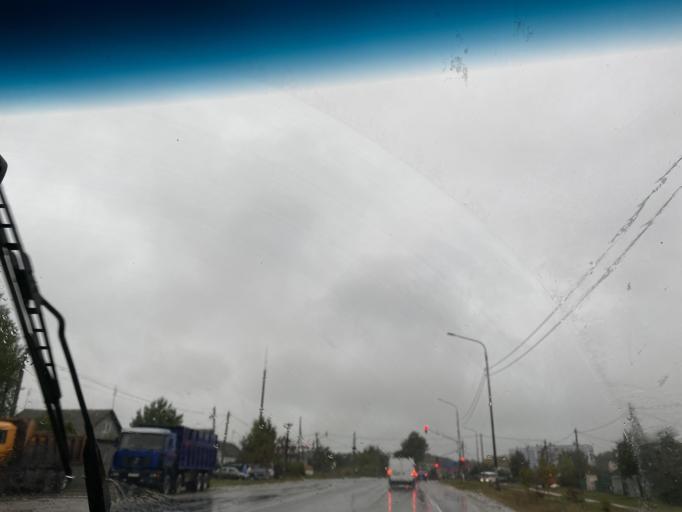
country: RU
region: Rjazan
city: Ryazan'
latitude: 54.5252
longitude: 39.7867
